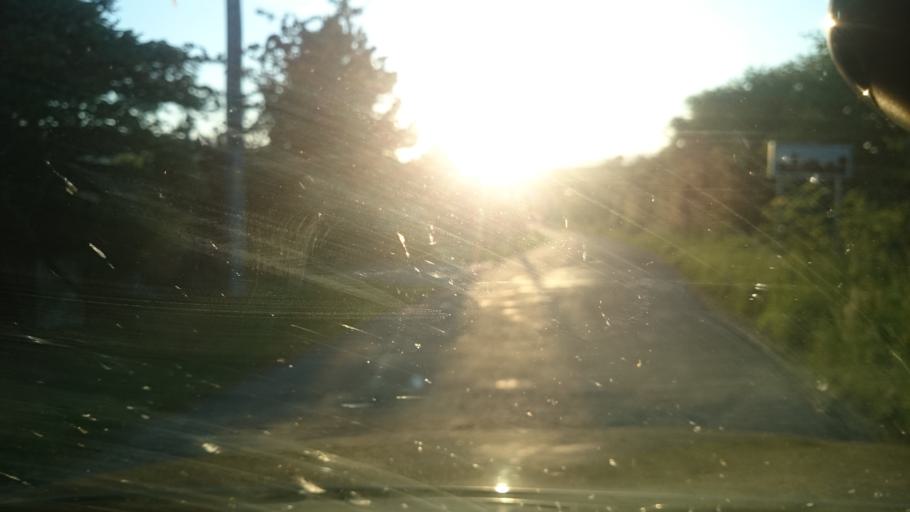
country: PL
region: Lower Silesian Voivodeship
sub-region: Powiat zabkowicki
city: Kamieniec Zabkowicki
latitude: 50.4897
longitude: 16.8314
